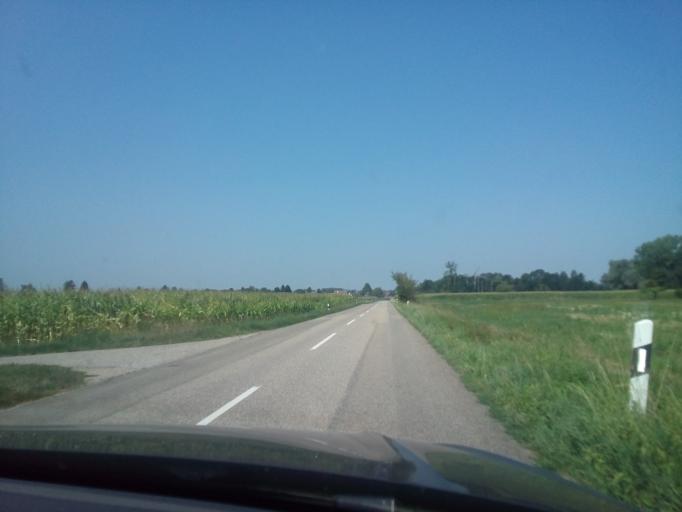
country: DE
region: Baden-Wuerttemberg
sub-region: Karlsruhe Region
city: Lichtenau
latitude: 48.6772
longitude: 7.9961
